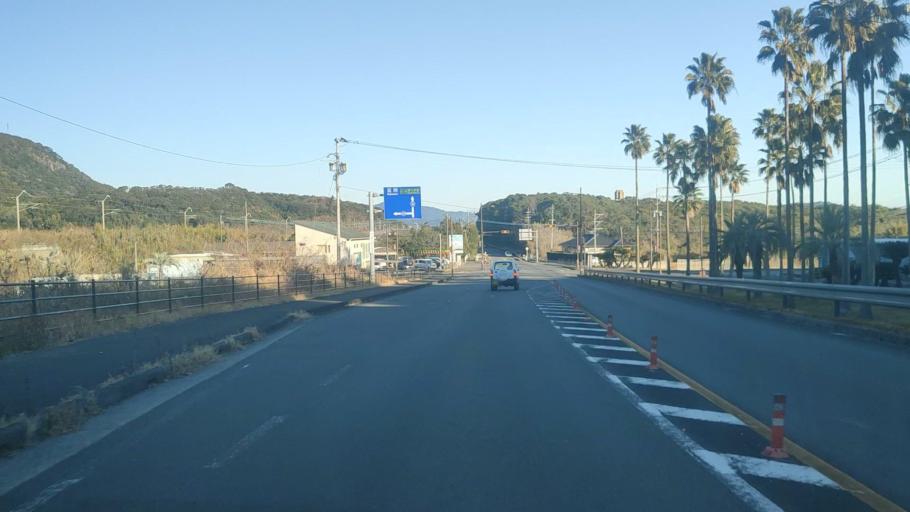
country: JP
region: Miyazaki
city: Nobeoka
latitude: 32.3786
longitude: 131.6276
